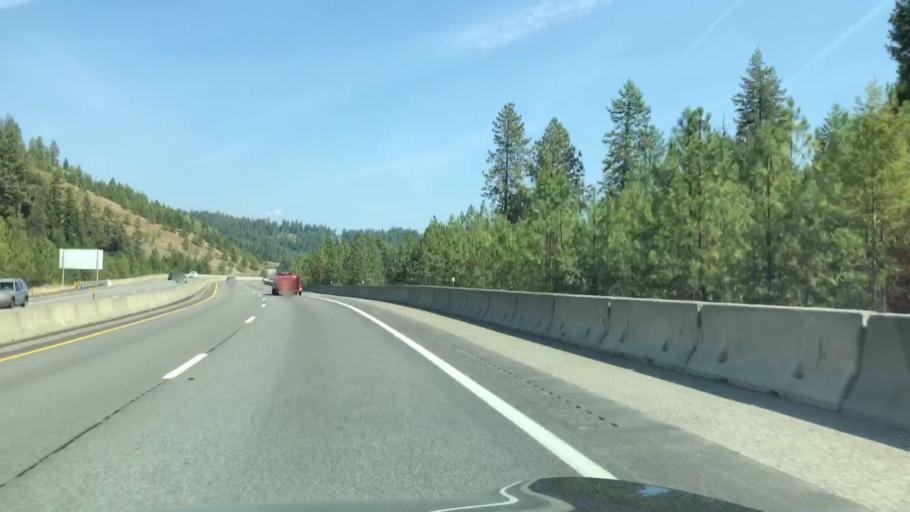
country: US
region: Idaho
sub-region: Kootenai County
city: Coeur d'Alene
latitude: 47.6622
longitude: -116.7435
